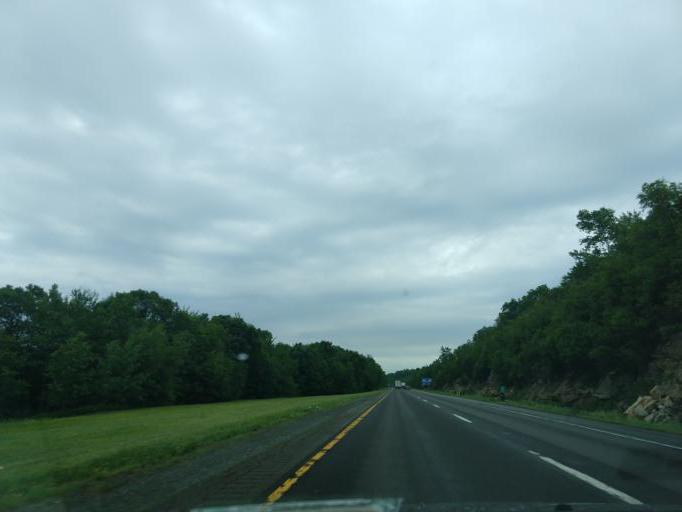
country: US
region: Pennsylvania
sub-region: Luzerne County
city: West Hazleton
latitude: 40.9554
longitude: -76.0277
